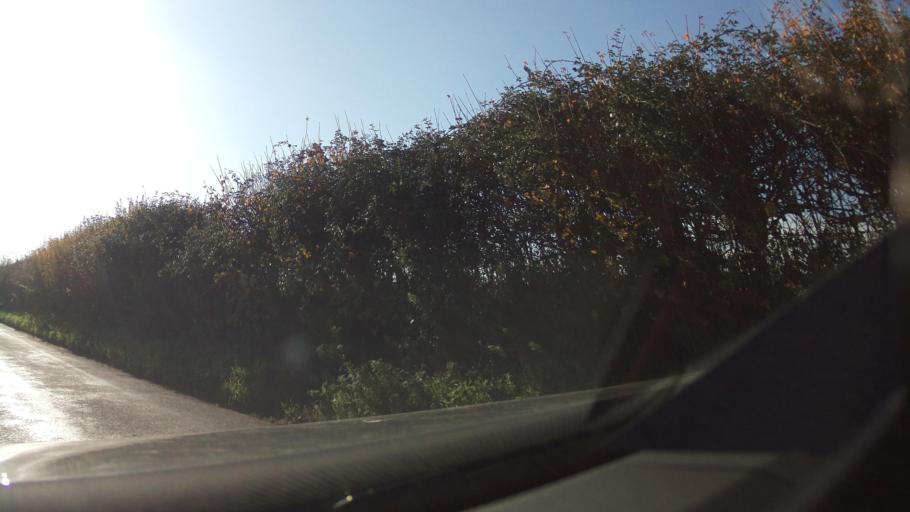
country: GB
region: England
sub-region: Dorset
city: Sherborne
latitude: 50.9859
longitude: -2.5159
